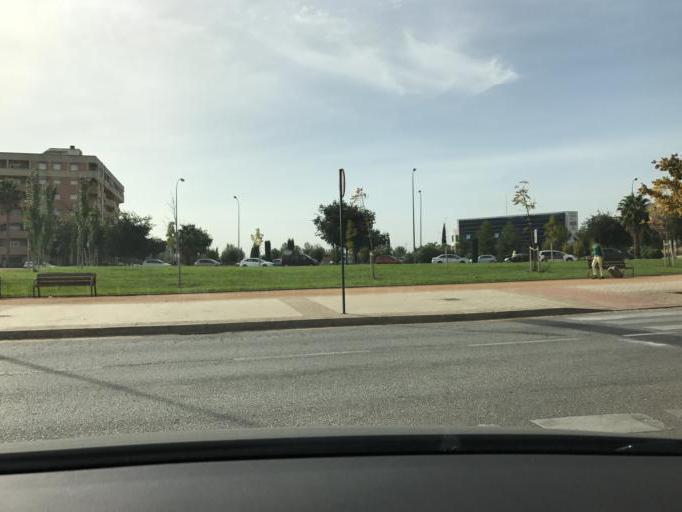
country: ES
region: Andalusia
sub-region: Provincia de Granada
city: Granada
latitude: 37.1966
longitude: -3.6202
